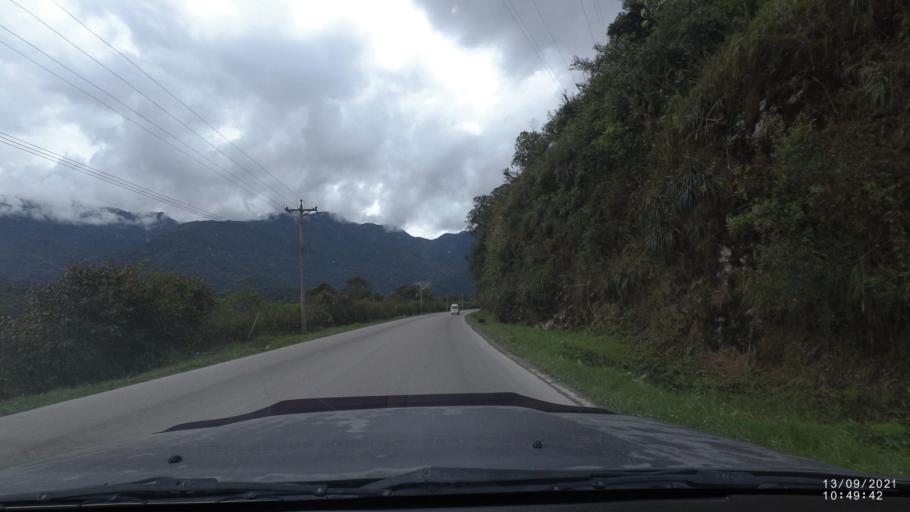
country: BO
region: Cochabamba
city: Colomi
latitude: -17.1986
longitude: -65.8567
